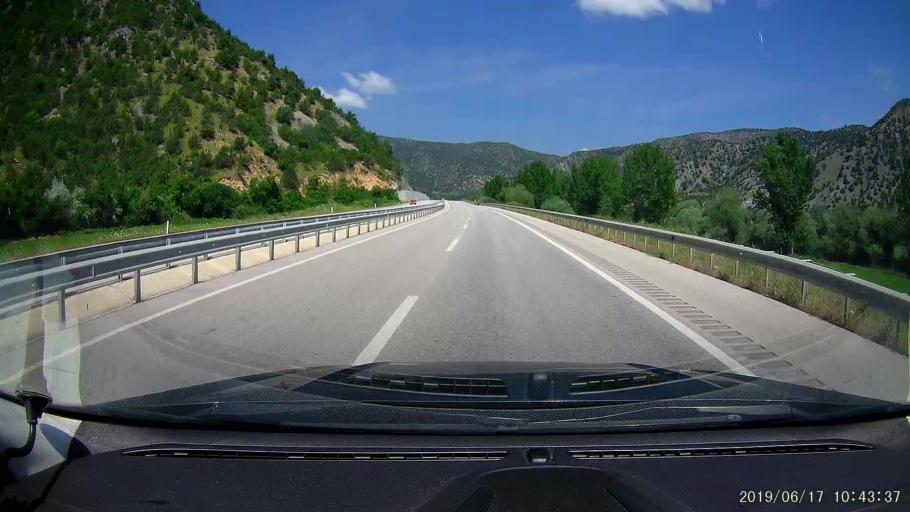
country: TR
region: Corum
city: Kargi
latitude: 41.0670
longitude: 34.5320
